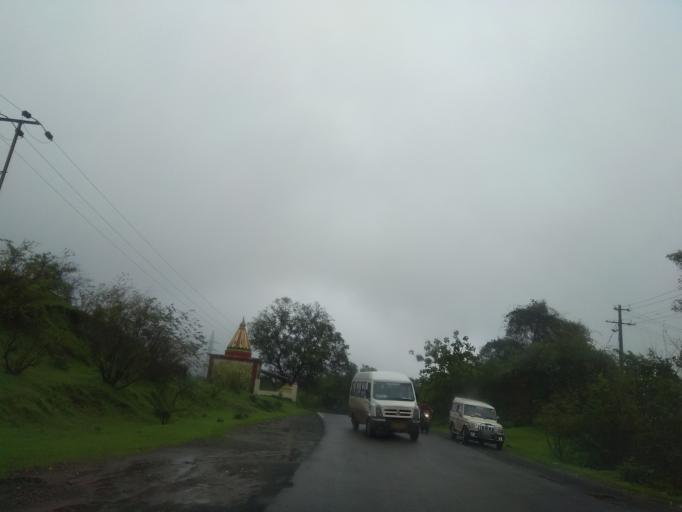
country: IN
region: Maharashtra
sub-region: Raigarh
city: Indapur
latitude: 18.4923
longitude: 73.4224
